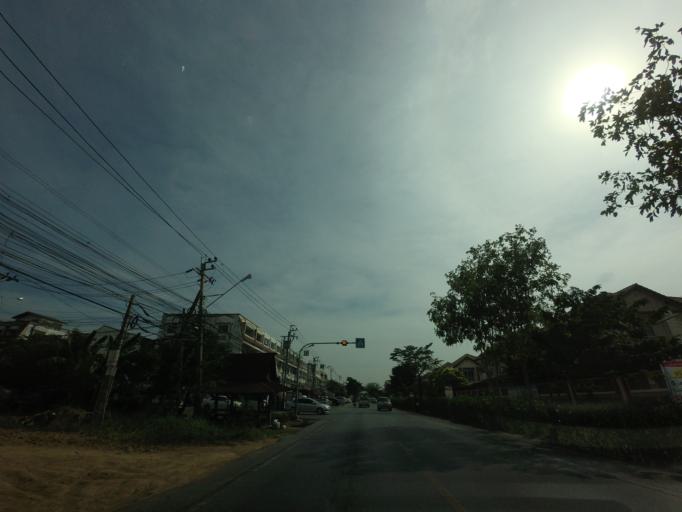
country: TH
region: Bangkok
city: Khan Na Yao
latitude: 13.8624
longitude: 100.6926
